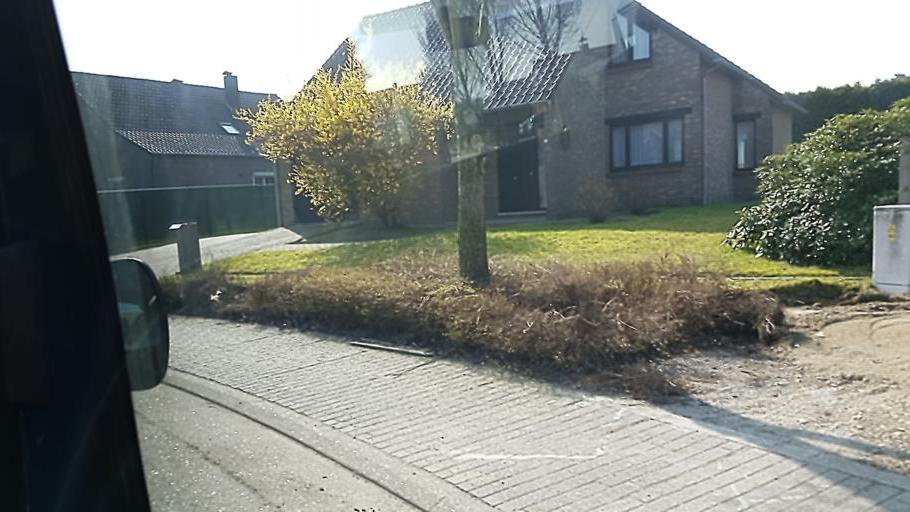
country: BE
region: Flanders
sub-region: Provincie Limburg
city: Genk
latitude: 51.0008
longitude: 5.4991
